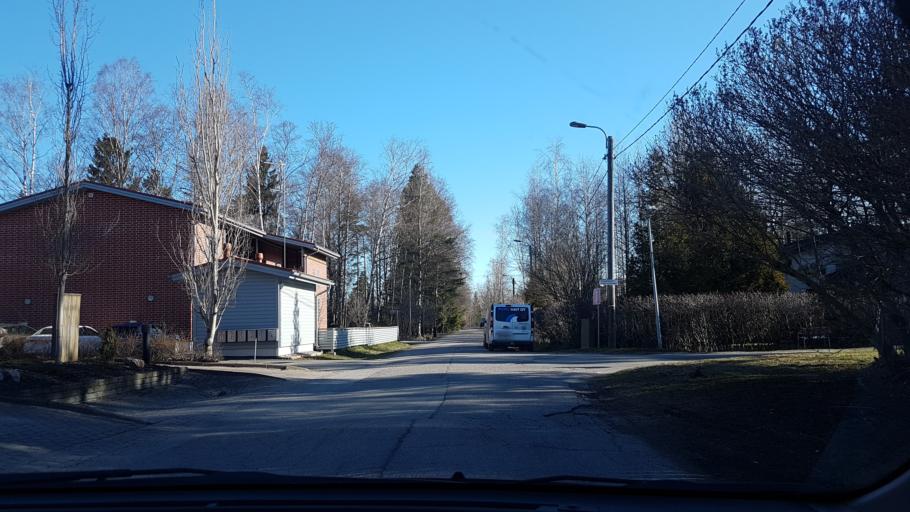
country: FI
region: Uusimaa
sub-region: Helsinki
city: Vantaa
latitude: 60.2690
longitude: 25.0922
